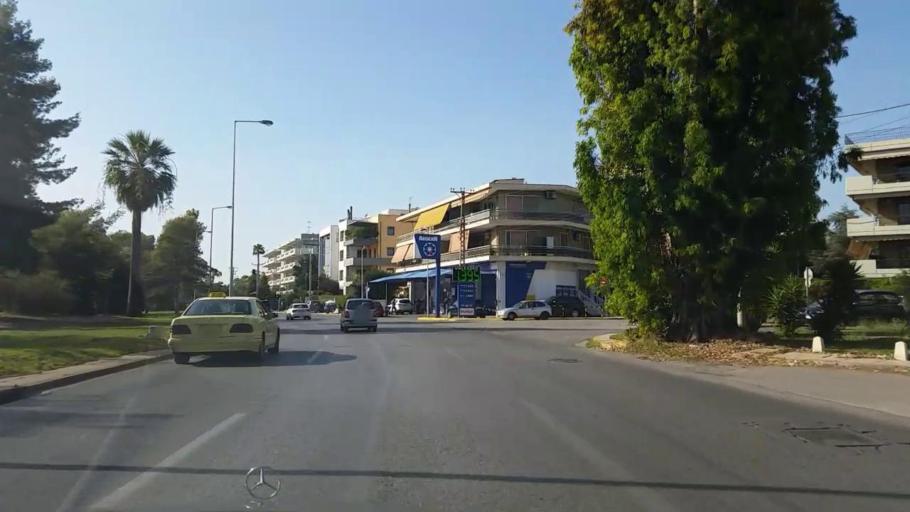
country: GR
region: Attica
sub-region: Nomarchia Athinas
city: Glyfada
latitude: 37.8515
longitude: 23.7529
